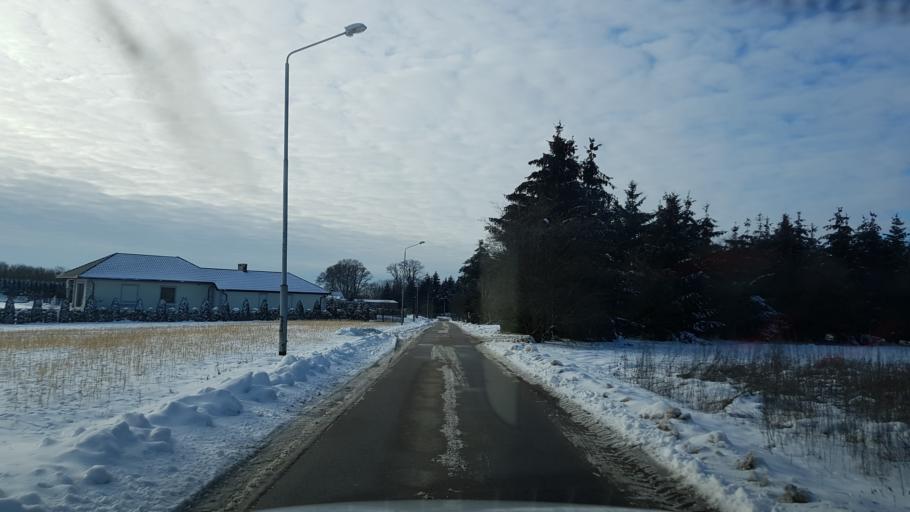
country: PL
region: West Pomeranian Voivodeship
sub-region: Powiat drawski
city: Drawsko Pomorskie
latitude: 53.5404
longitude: 15.7915
